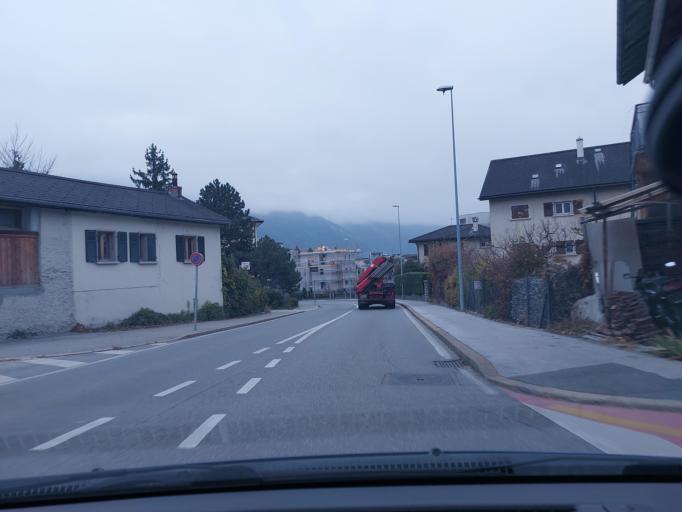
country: CH
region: Valais
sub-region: Sierre District
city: Sierre
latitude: 46.2962
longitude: 7.5332
